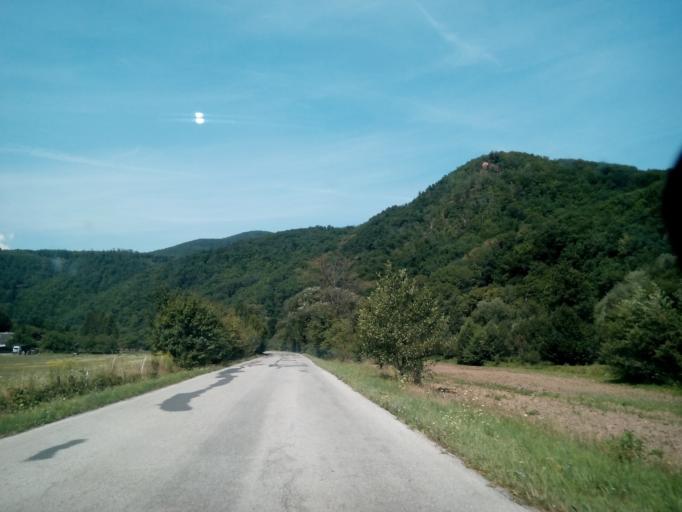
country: SK
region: Presovsky
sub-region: Okres Presov
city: Presov
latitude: 48.8641
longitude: 21.2094
